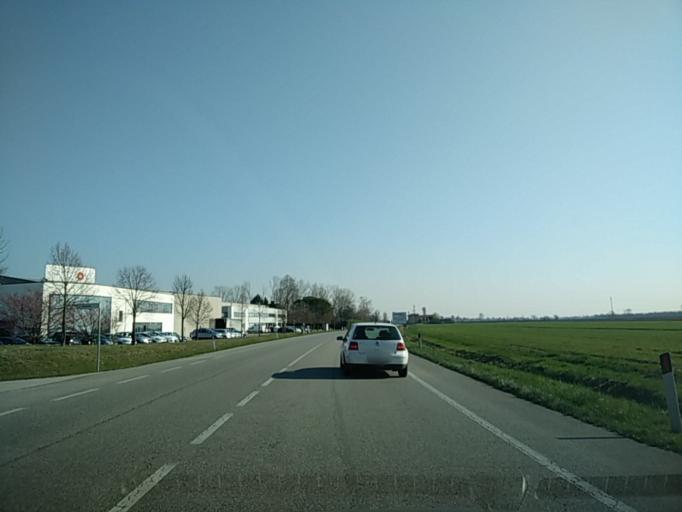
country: IT
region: Friuli Venezia Giulia
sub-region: Provincia di Pordenone
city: Villotta
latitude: 45.8787
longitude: 12.7804
